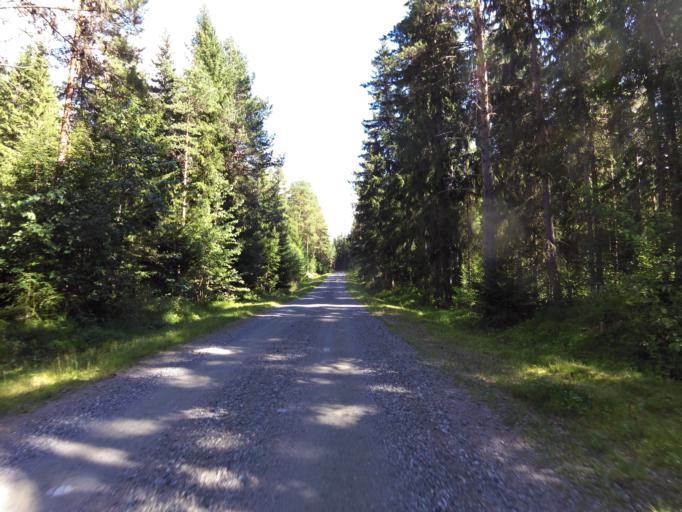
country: SE
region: Dalarna
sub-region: Faluns Kommun
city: Svardsjo
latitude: 60.6612
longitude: 15.8605
